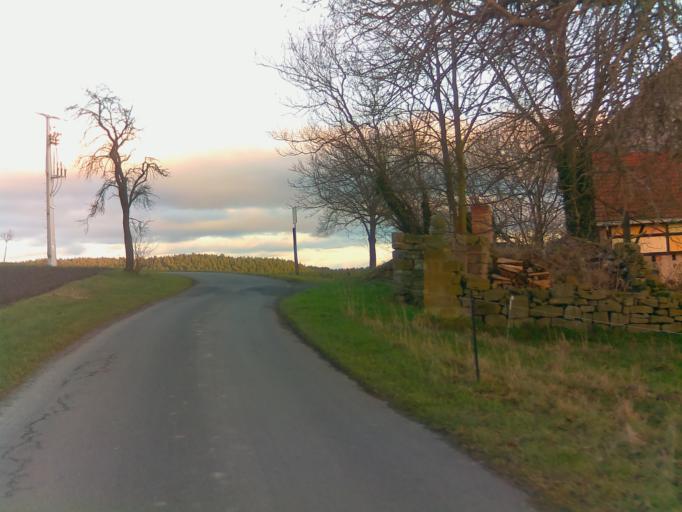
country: DE
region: Thuringia
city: Rudolstadt
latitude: 50.7606
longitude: 11.3520
